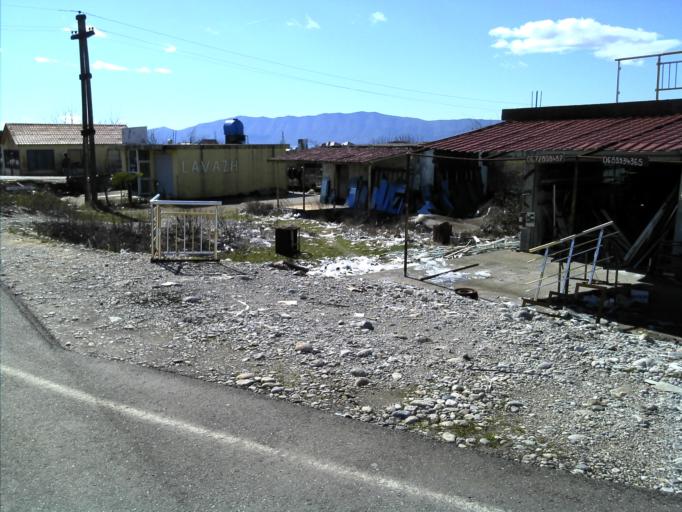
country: AL
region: Shkoder
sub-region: Rrethi i Malesia e Madhe
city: Grude-Fushe
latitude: 42.1652
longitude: 19.4687
